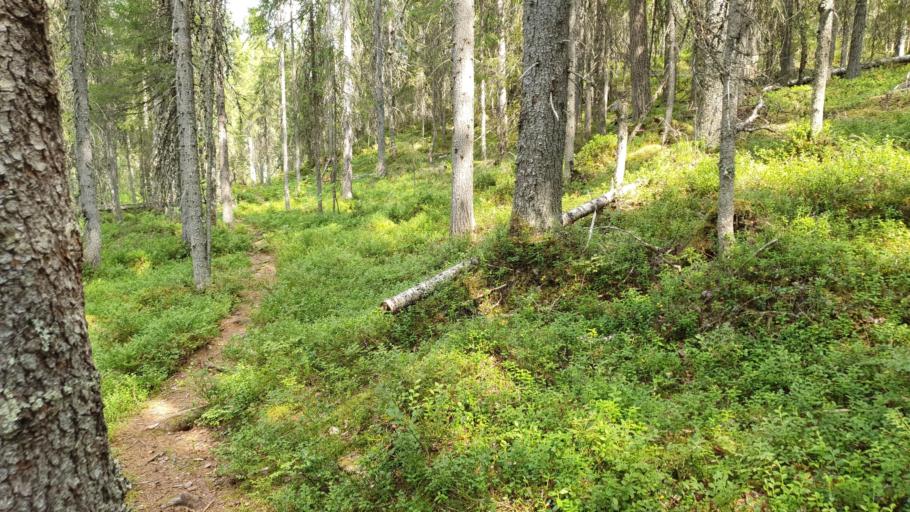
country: FI
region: Kainuu
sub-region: Kehys-Kainuu
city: Kuhmo
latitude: 64.2972
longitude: 29.2638
